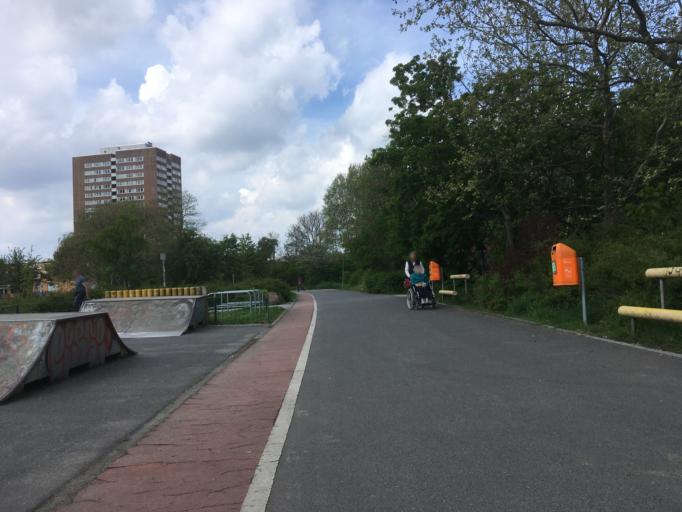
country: DE
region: Berlin
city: Marzahn
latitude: 52.5518
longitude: 13.5616
